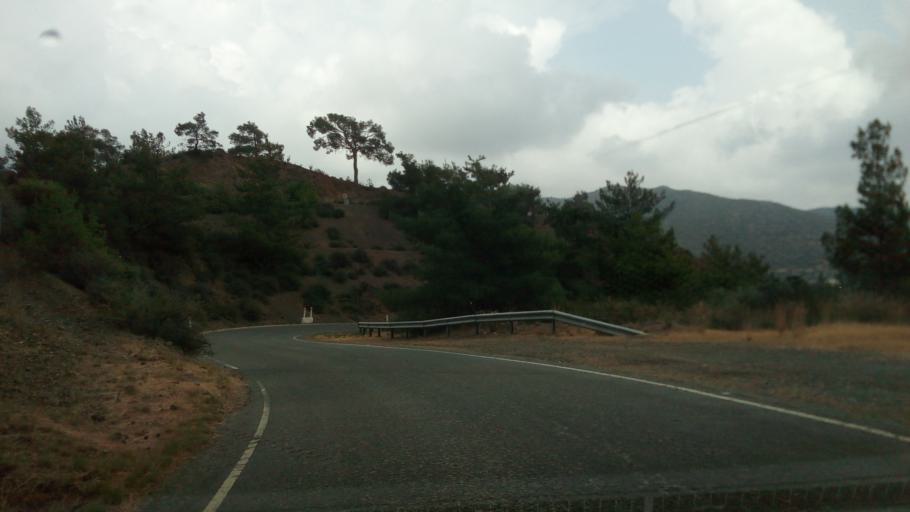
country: CY
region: Limassol
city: Parekklisha
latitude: 34.8641
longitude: 33.1828
